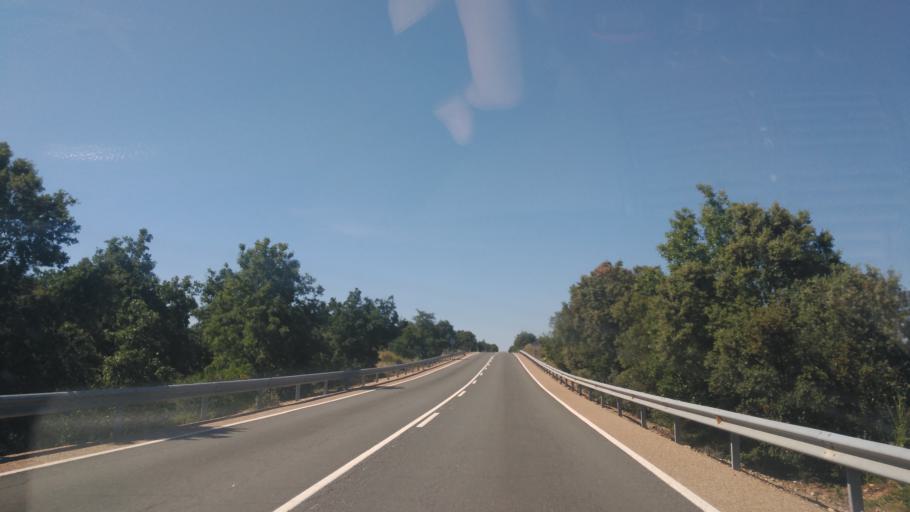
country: ES
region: Castille and Leon
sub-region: Provincia de Zamora
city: Cuelgamures
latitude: 41.2708
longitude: -5.7156
